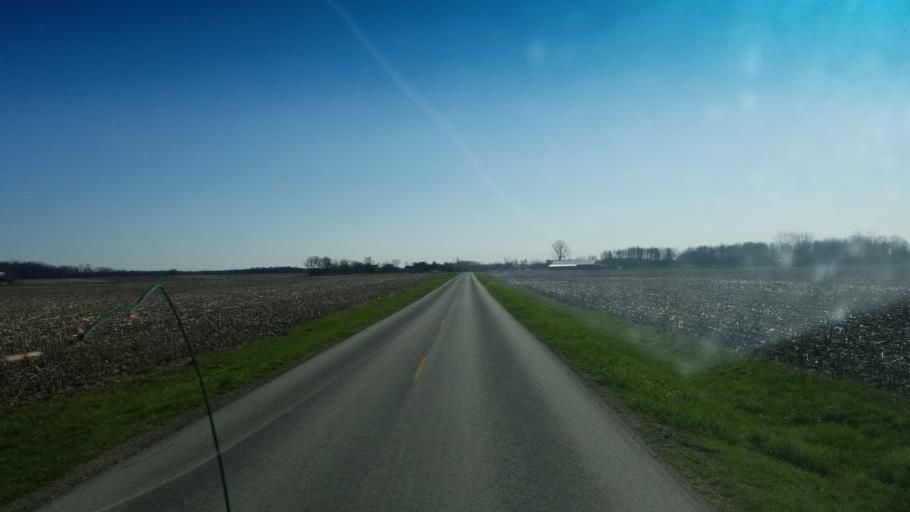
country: US
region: Ohio
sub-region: Hardin County
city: Kenton
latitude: 40.5405
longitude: -83.6105
